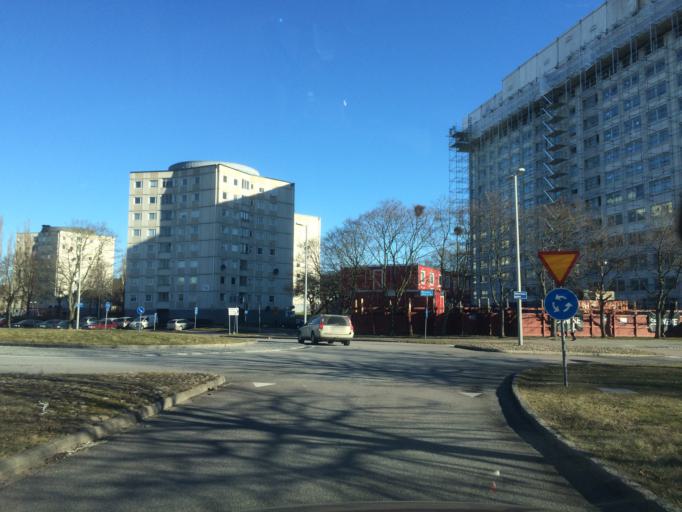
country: SE
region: Vaestra Goetaland
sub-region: Goteborg
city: Majorna
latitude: 57.6522
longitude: 11.9069
